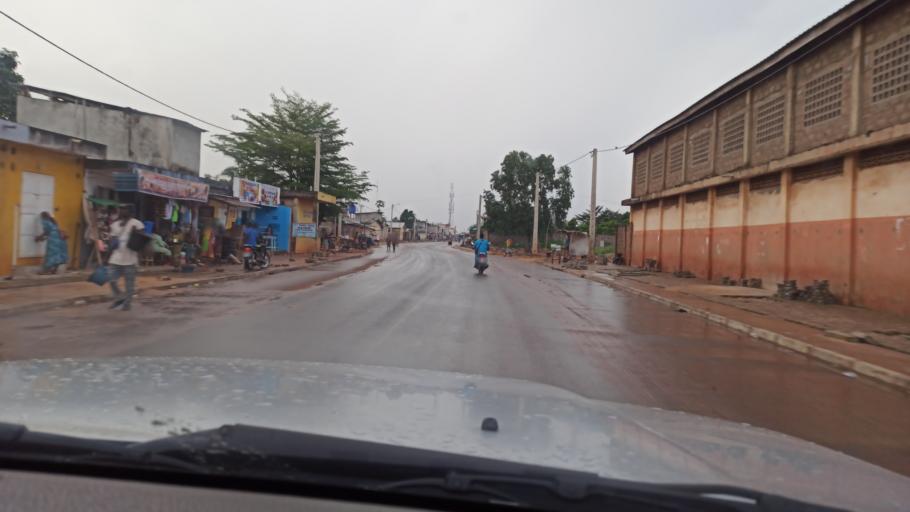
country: BJ
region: Queme
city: Porto-Novo
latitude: 6.4949
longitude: 2.6434
